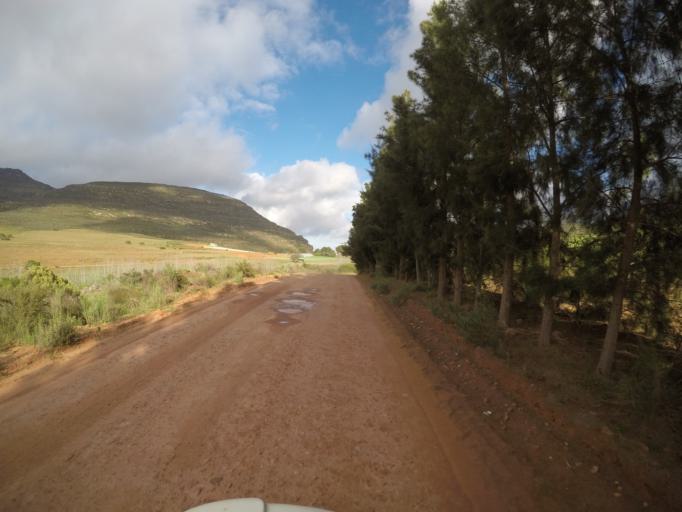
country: ZA
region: Western Cape
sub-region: West Coast District Municipality
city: Clanwilliam
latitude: -32.3404
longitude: 18.8005
